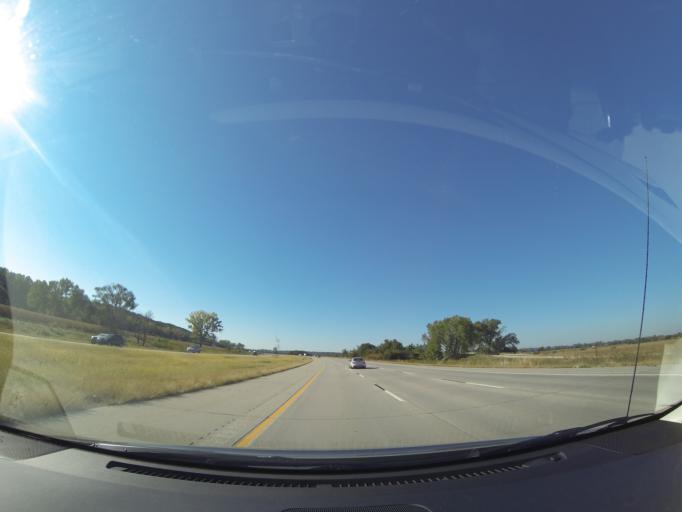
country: US
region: Nebraska
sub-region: Saunders County
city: Ashland
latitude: 41.0611
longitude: -96.2944
